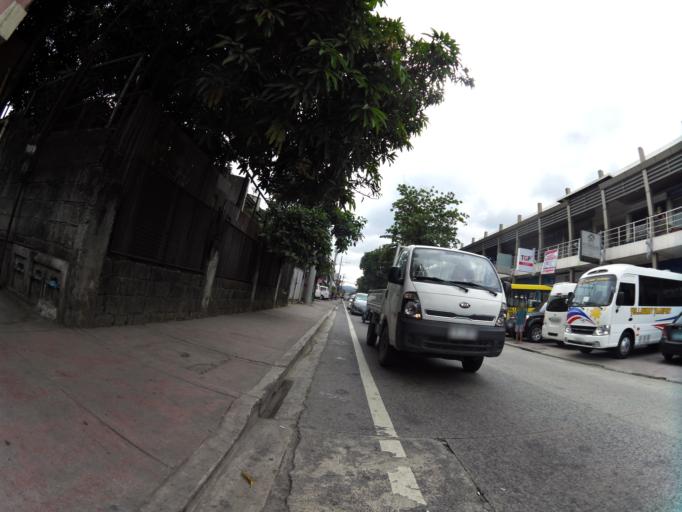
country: PH
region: Calabarzon
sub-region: Province of Rizal
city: Antipolo
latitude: 14.6421
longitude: 121.1109
